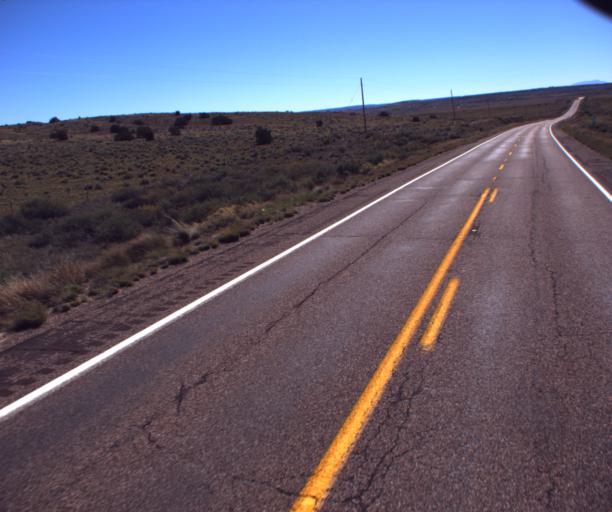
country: US
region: Arizona
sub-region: Apache County
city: Saint Johns
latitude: 34.5298
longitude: -109.4590
